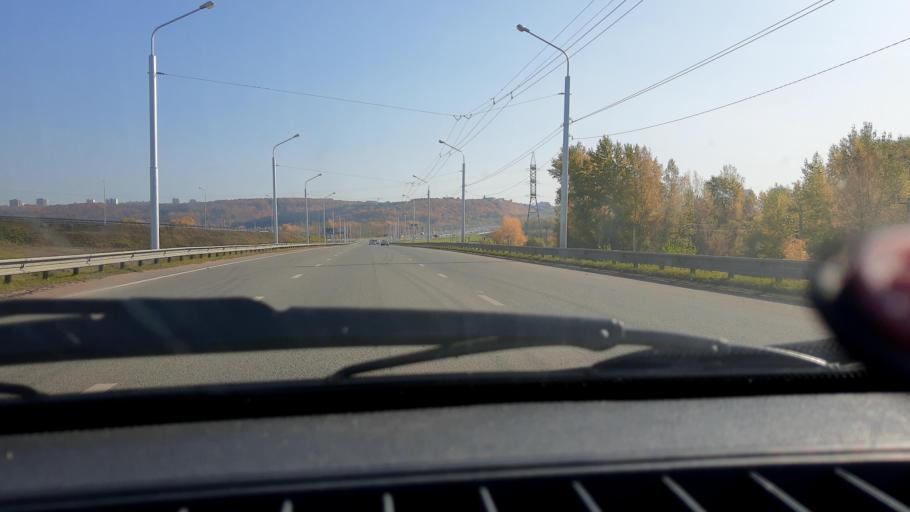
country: RU
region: Bashkortostan
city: Ufa
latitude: 54.7641
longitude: 55.9514
